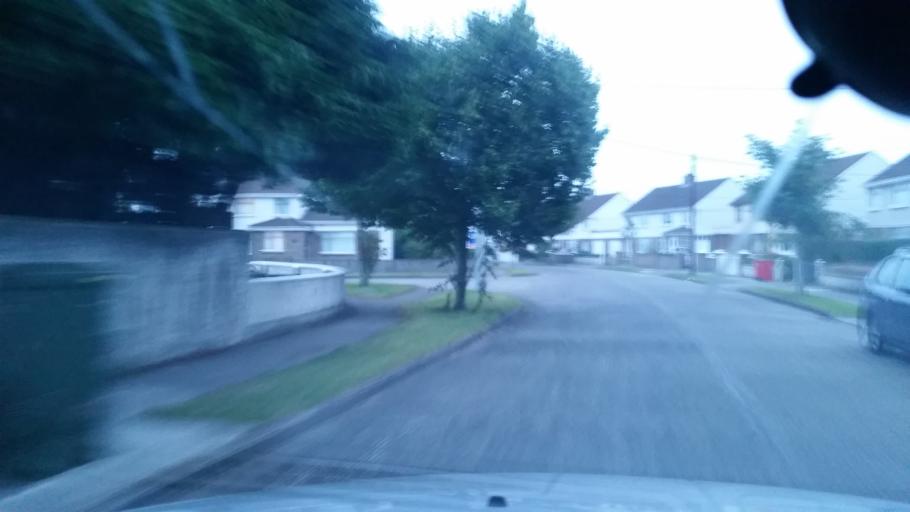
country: IE
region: Leinster
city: Beaumont
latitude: 53.3924
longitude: -6.2378
